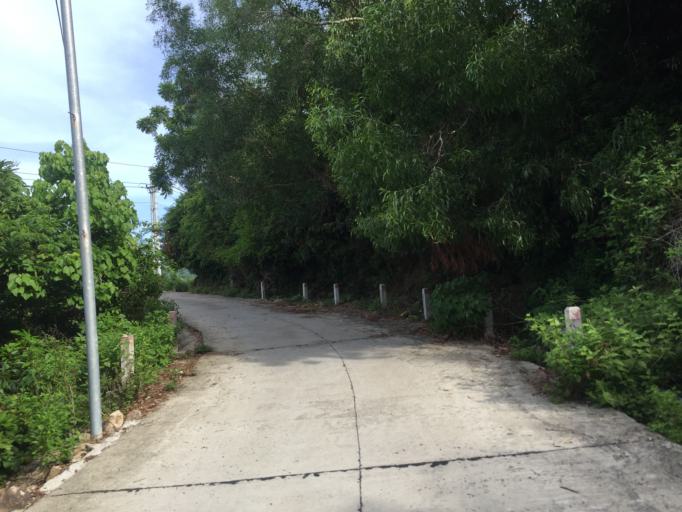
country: VN
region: Quang Nam
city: Hoi An
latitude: 15.9558
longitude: 108.5090
